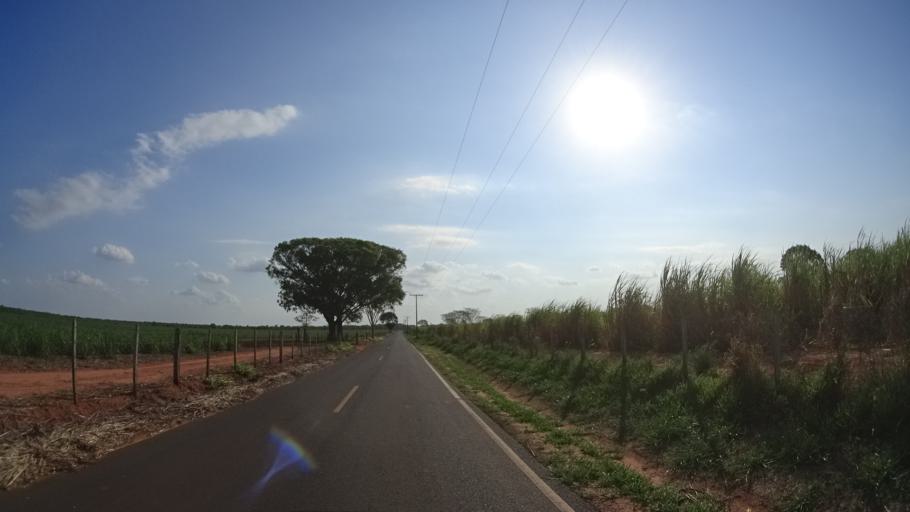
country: BR
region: Sao Paulo
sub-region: Urupes
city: Urupes
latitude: -21.3894
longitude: -49.5016
